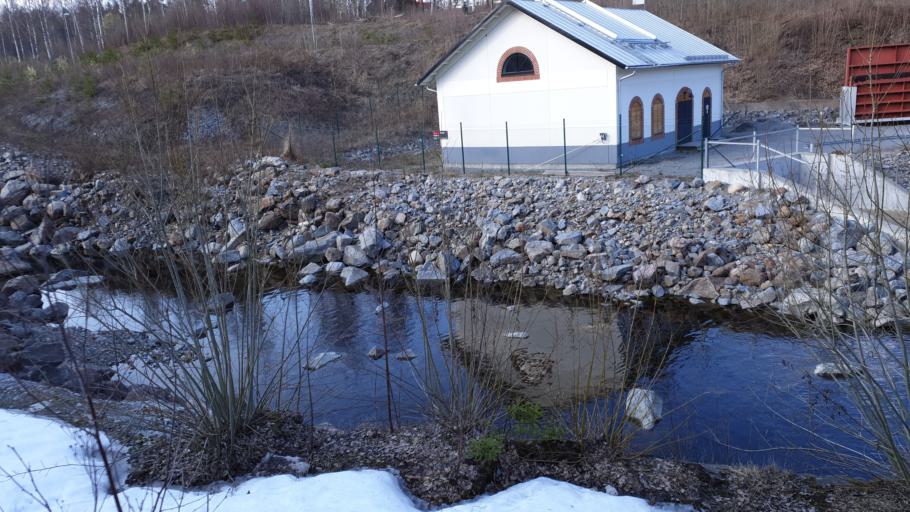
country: SE
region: Gaevleborg
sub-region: Hudiksvalls Kommun
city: Iggesund
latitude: 61.6391
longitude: 17.0745
